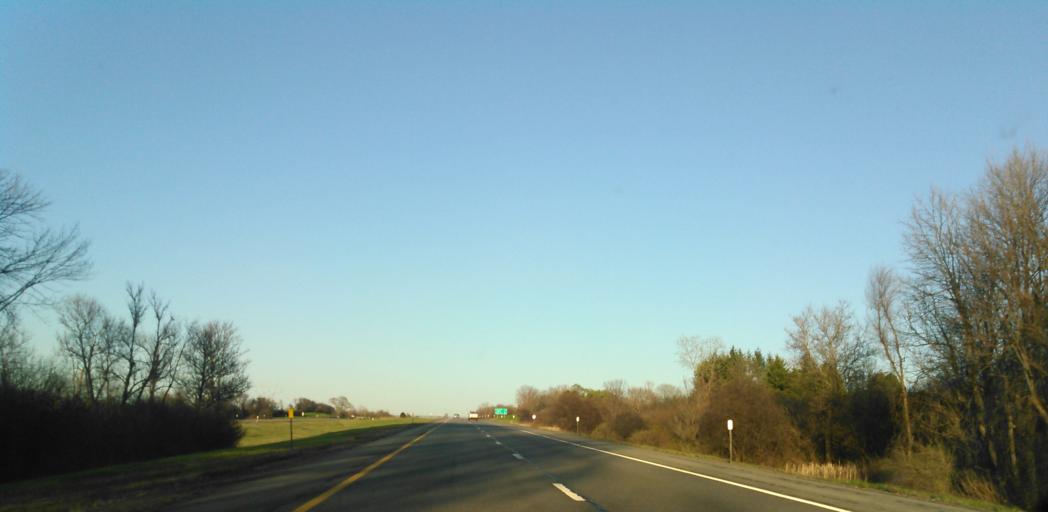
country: US
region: New York
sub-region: Monroe County
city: Honeoye Falls
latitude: 43.0468
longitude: -77.6088
